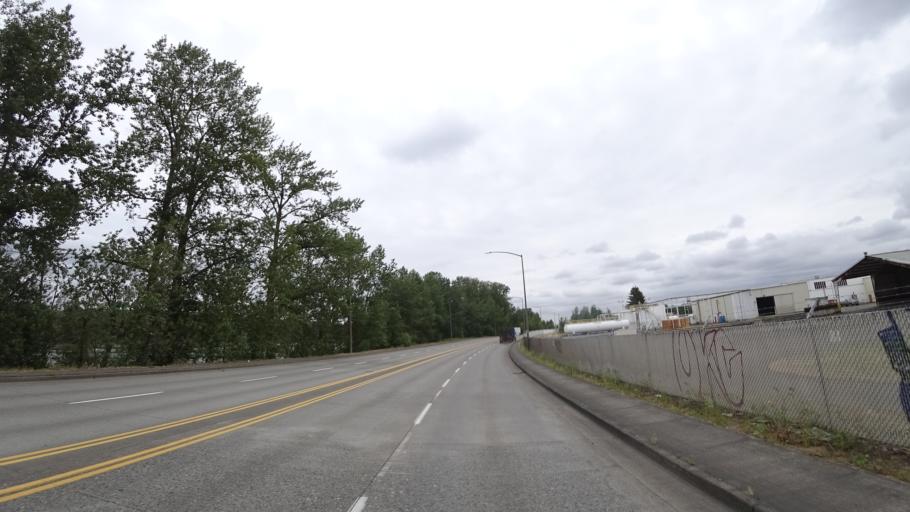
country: US
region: Washington
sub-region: Clark County
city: Vancouver
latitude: 45.6174
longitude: -122.7130
